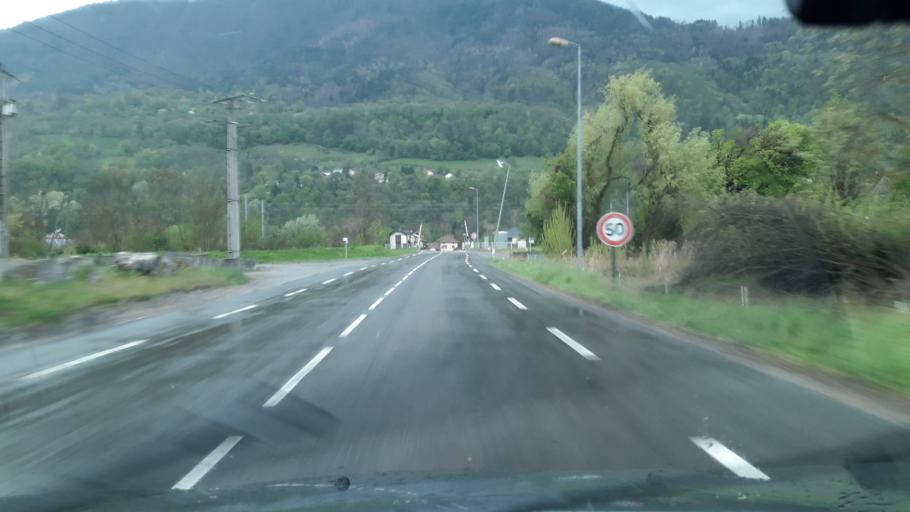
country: FR
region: Rhone-Alpes
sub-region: Departement de l'Isere
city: Le Cheylas
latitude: 45.3941
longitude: 5.9962
